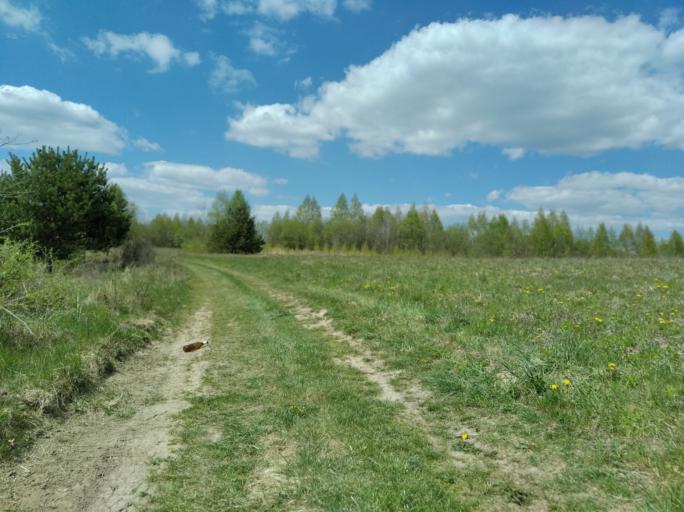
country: PL
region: Subcarpathian Voivodeship
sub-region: Powiat brzozowski
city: Wesola
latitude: 49.7470
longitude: 22.0822
